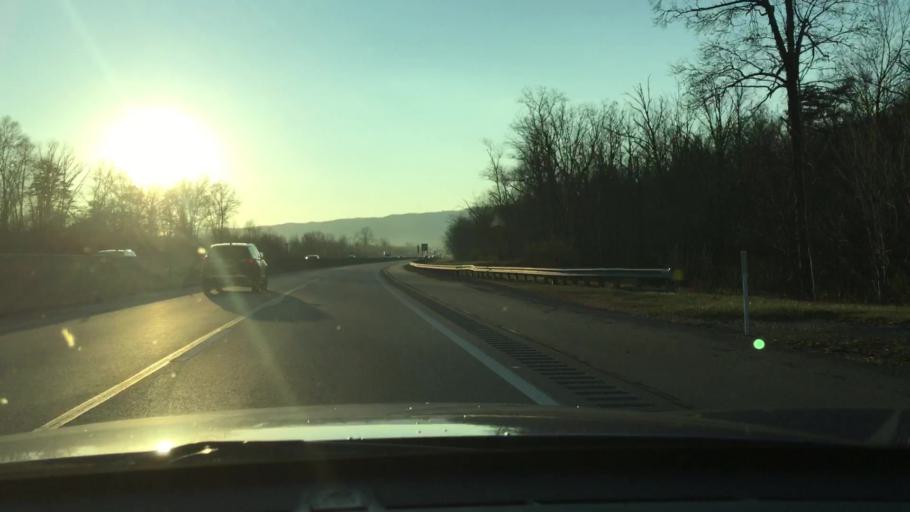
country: US
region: Pennsylvania
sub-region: Franklin County
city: Doylestown
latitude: 40.1274
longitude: -77.7494
